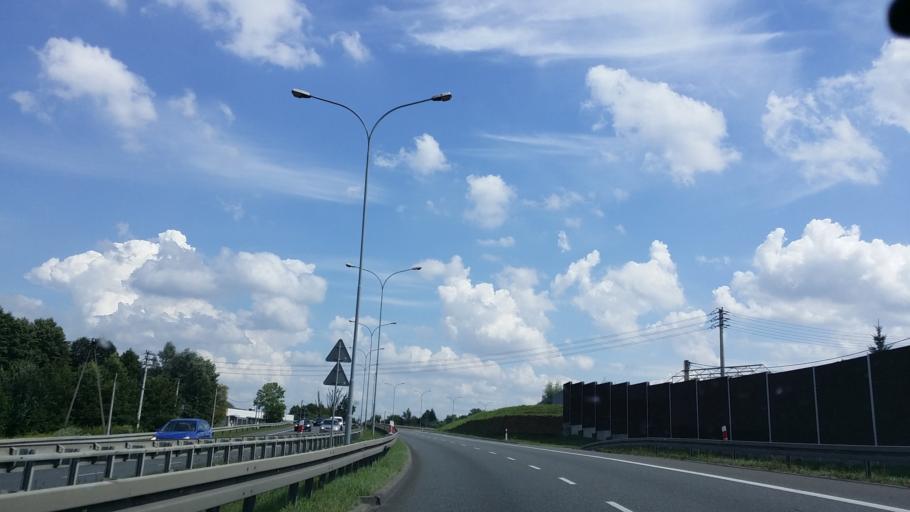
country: PL
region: Lesser Poland Voivodeship
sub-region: Powiat wielicki
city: Wieliczka
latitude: 49.9982
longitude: 20.0299
